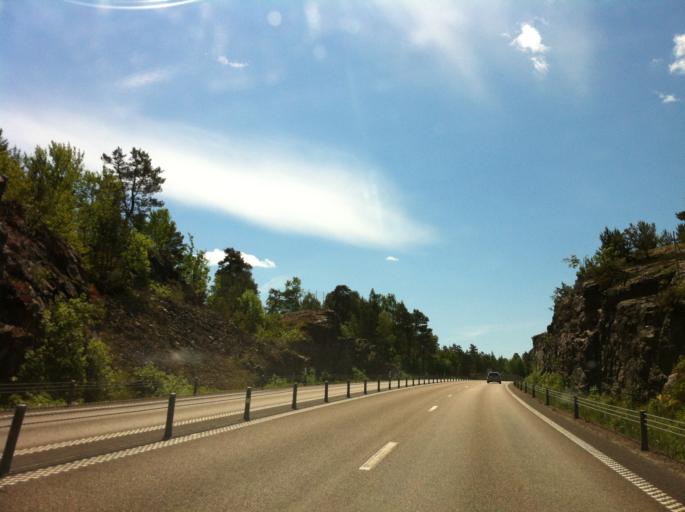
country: SE
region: Vaestra Goetaland
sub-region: Melleruds Kommun
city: Mellerud
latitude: 58.7627
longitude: 12.4896
